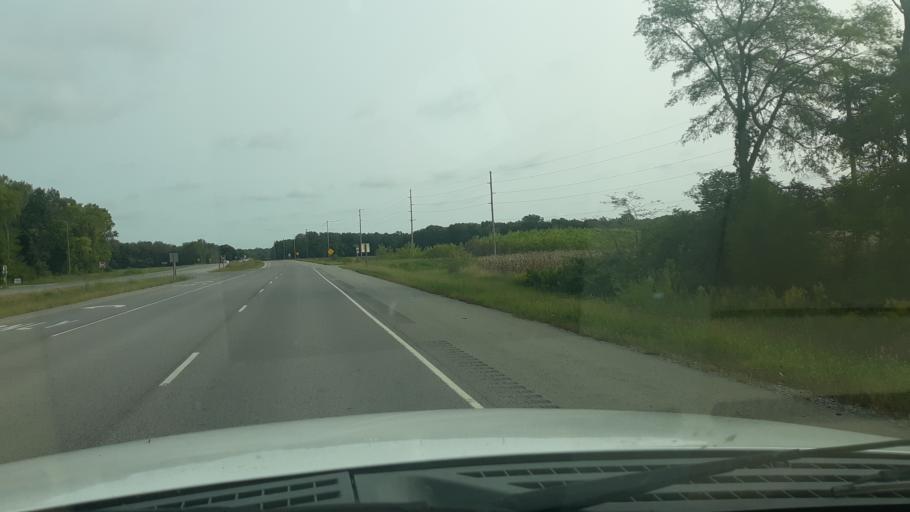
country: US
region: Illinois
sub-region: Saline County
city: Eldorado
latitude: 37.8769
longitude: -88.3935
